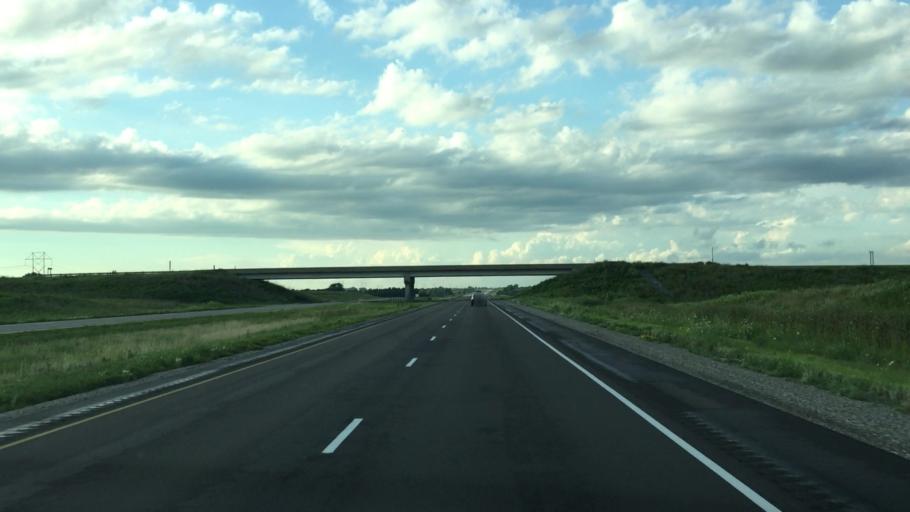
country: US
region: Iowa
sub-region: Washington County
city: Washington
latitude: 41.3353
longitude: -91.5519
